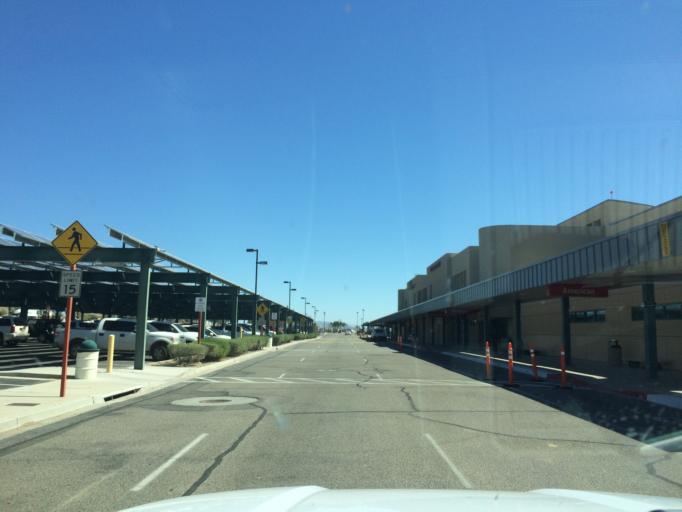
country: US
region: Arizona
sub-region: Yuma County
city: Yuma
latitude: 32.6686
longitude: -114.6000
